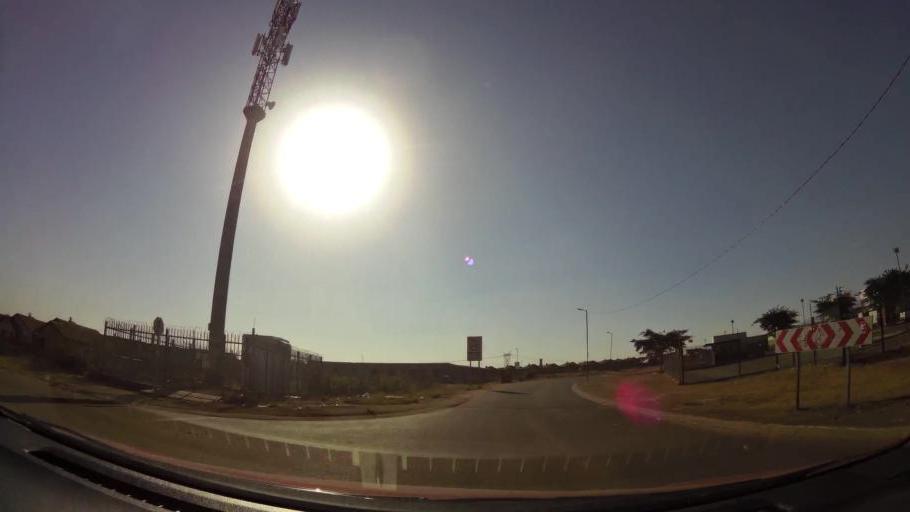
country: ZA
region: Gauteng
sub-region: City of Tshwane Metropolitan Municipality
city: Mabopane
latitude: -25.5709
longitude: 28.0962
